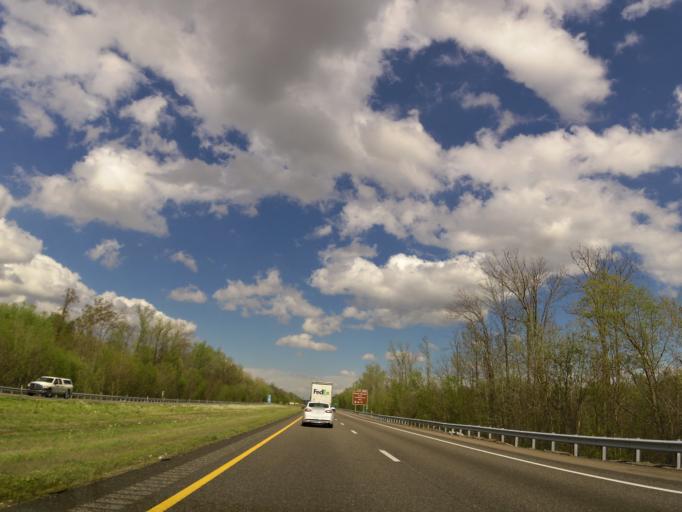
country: US
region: Tennessee
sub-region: Madison County
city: Jackson
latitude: 35.6494
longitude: -88.8935
